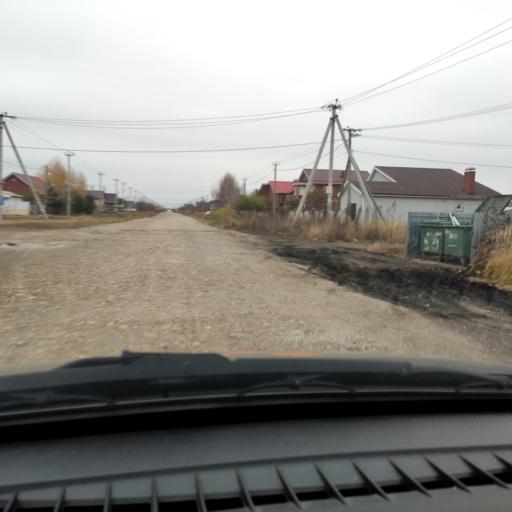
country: RU
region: Samara
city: Podstepki
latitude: 53.5230
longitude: 49.1540
